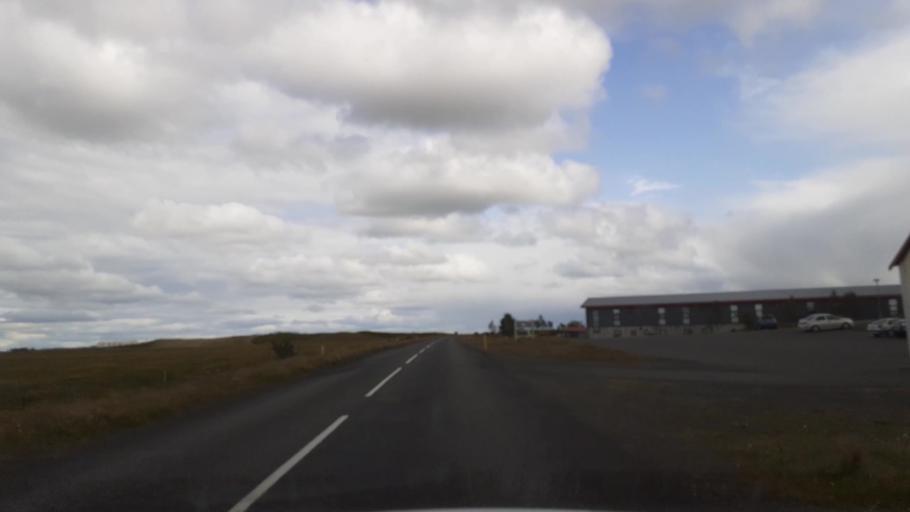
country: IS
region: South
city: Vestmannaeyjar
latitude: 63.8311
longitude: -20.4233
